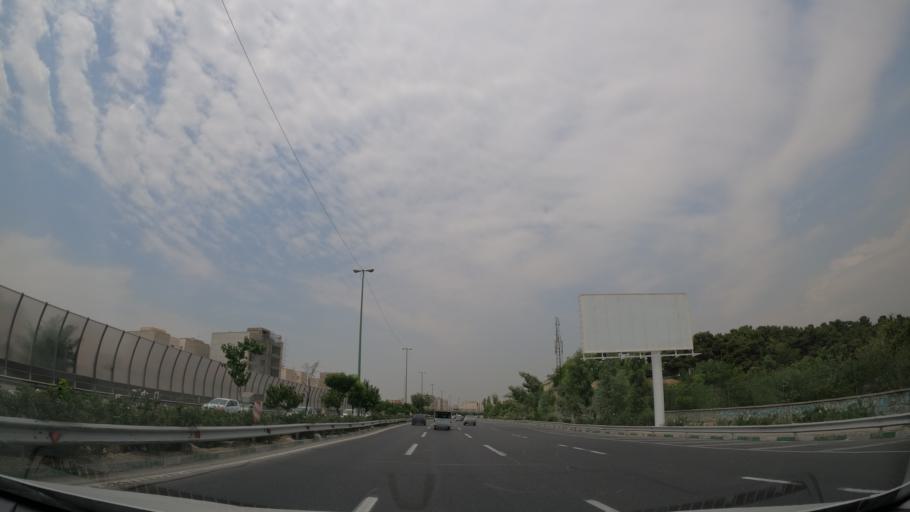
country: IR
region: Tehran
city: Tehran
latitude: 35.7391
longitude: 51.3650
